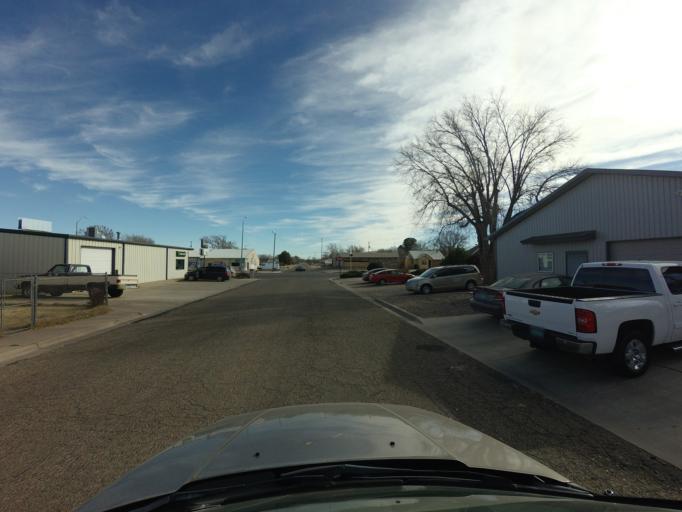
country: US
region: New Mexico
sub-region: Curry County
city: Clovis
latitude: 34.4110
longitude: -103.1971
